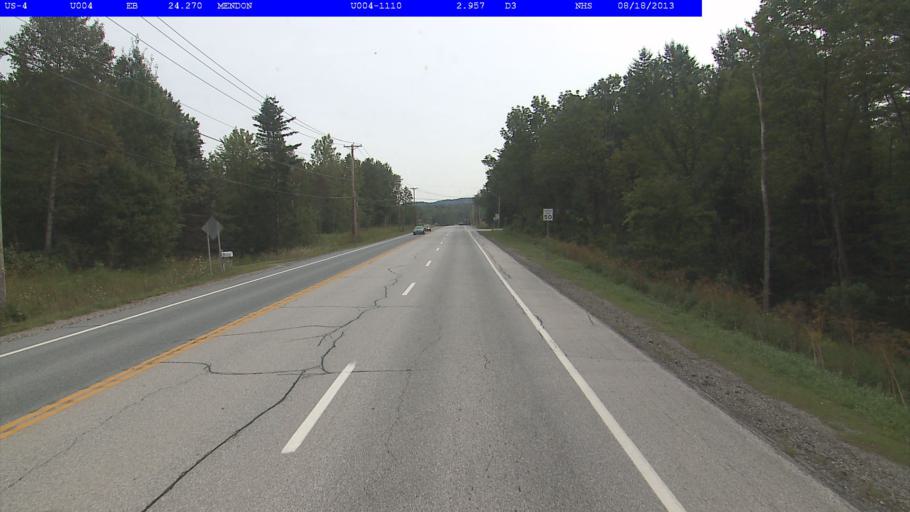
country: US
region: Vermont
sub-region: Rutland County
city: Rutland
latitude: 43.6501
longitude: -72.8959
